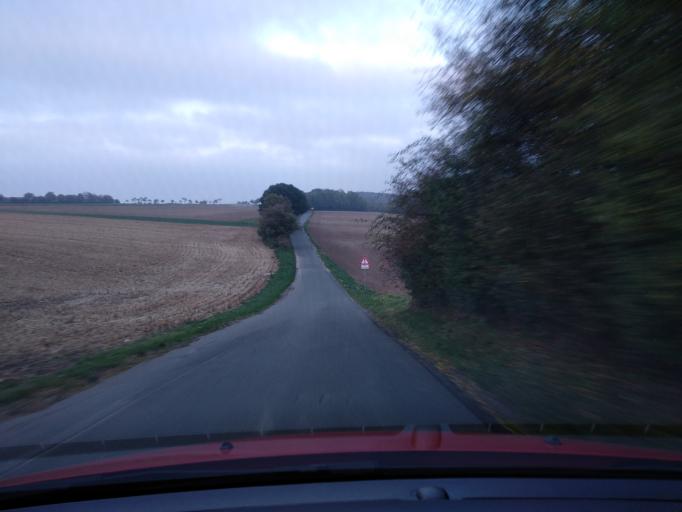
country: DE
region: North Rhine-Westphalia
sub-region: Regierungsbezirk Detmold
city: Paderborn
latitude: 51.6818
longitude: 8.7740
